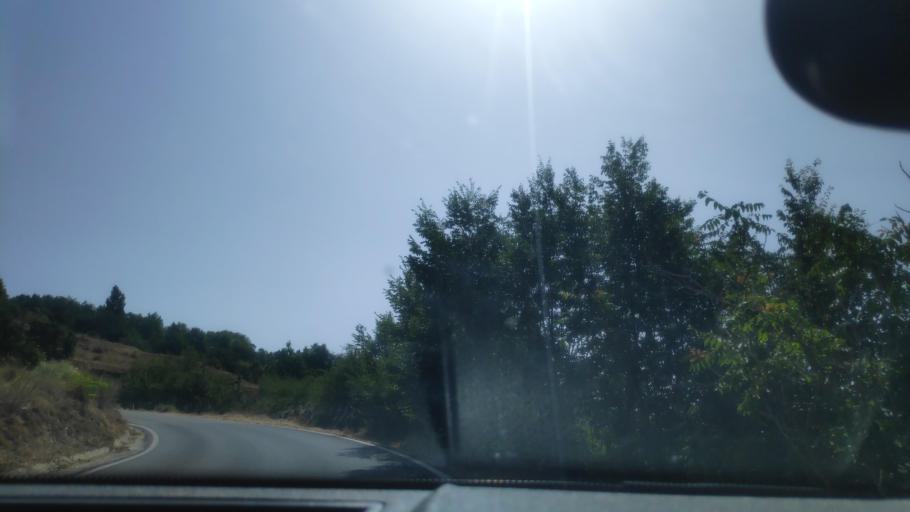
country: ES
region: Andalusia
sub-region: Provincia de Granada
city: Pampaneira
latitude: 36.9315
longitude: -3.3364
